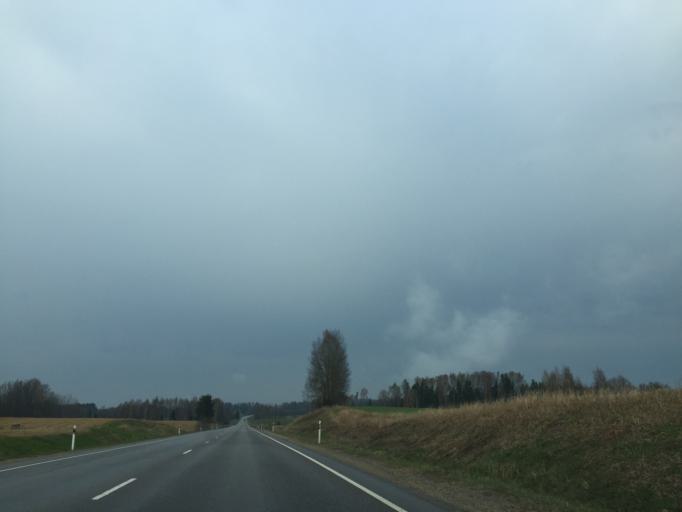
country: EE
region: Tartu
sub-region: UElenurme vald
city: Ulenurme
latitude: 58.1616
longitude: 26.6928
